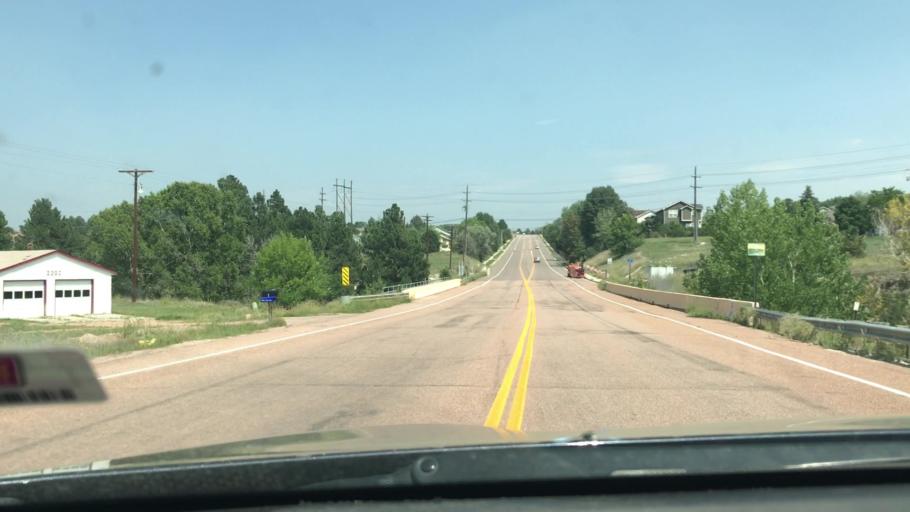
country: US
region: Colorado
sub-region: El Paso County
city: Gleneagle
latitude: 38.9808
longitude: -104.7857
